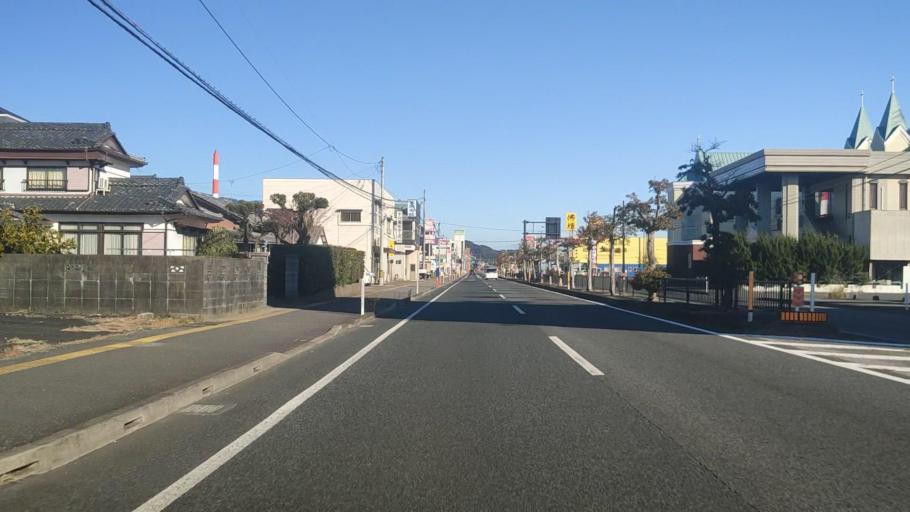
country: JP
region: Miyazaki
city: Nobeoka
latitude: 32.5908
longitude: 131.6759
